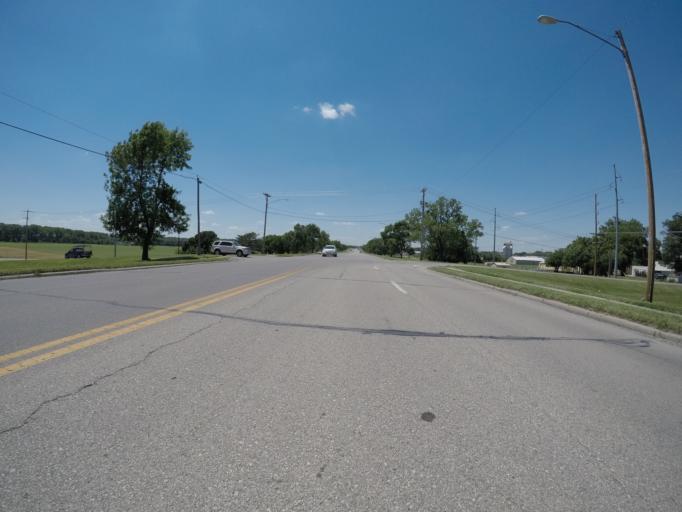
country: US
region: Kansas
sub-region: Geary County
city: Junction City
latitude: 39.0283
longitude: -96.8180
